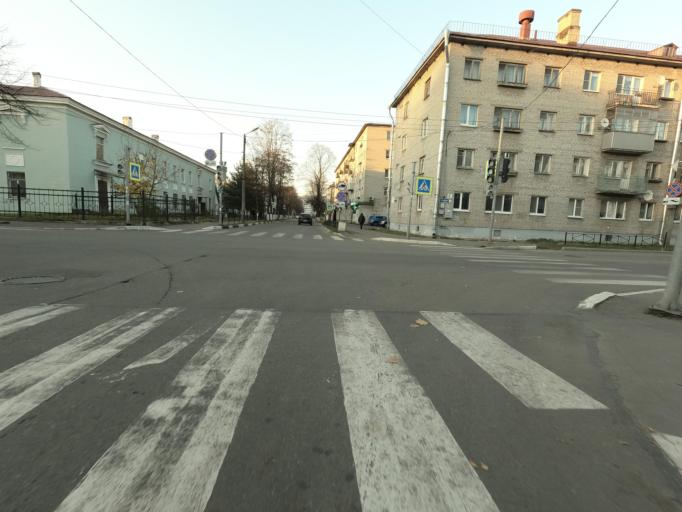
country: RU
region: Leningrad
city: Kirovsk
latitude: 59.8758
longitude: 30.9914
